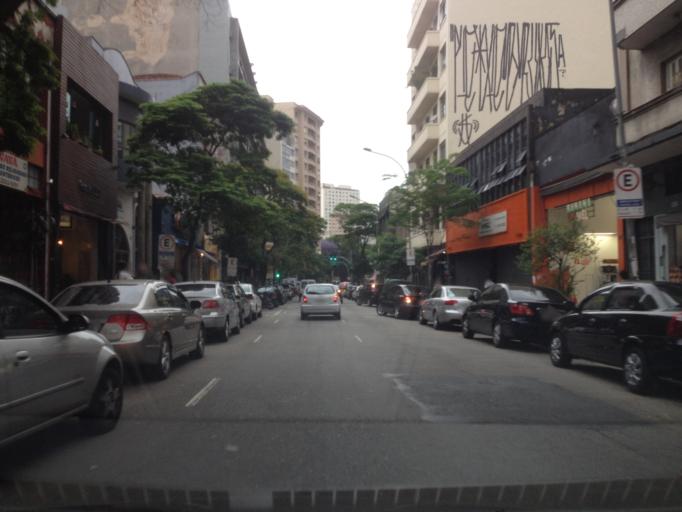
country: BR
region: Sao Paulo
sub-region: Sao Paulo
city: Sao Paulo
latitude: -23.5378
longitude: -46.6508
